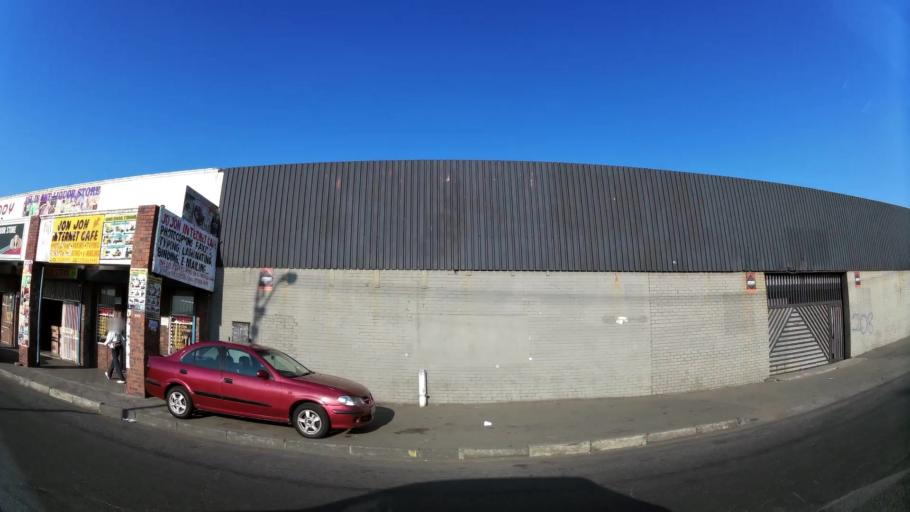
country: ZA
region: Gauteng
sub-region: Ekurhuleni Metropolitan Municipality
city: Germiston
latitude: -26.2178
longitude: 28.1743
